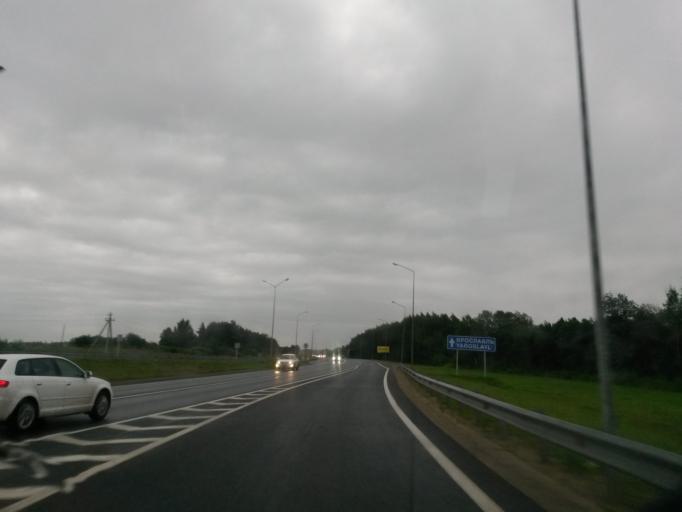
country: RU
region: Jaroslavl
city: Yaroslavl
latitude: 57.7364
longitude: 39.8962
